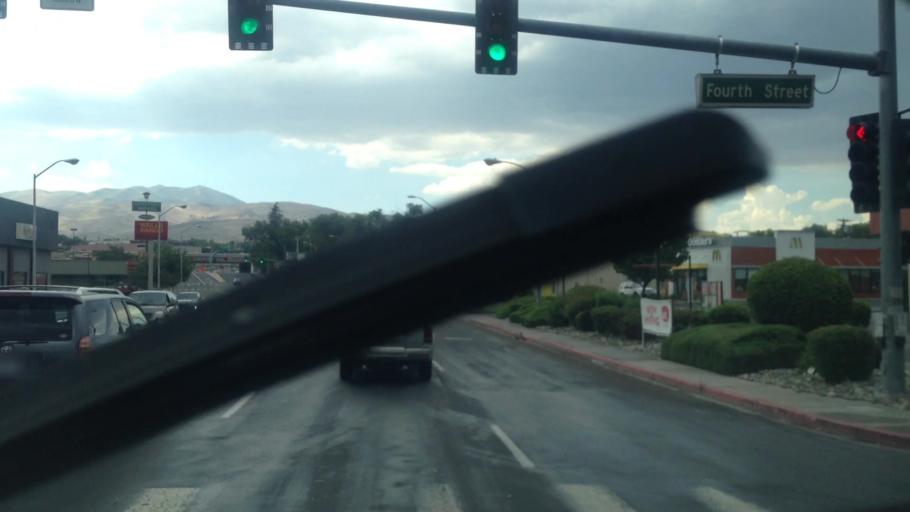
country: US
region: Nevada
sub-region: Washoe County
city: Reno
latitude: 39.5270
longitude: -119.8267
